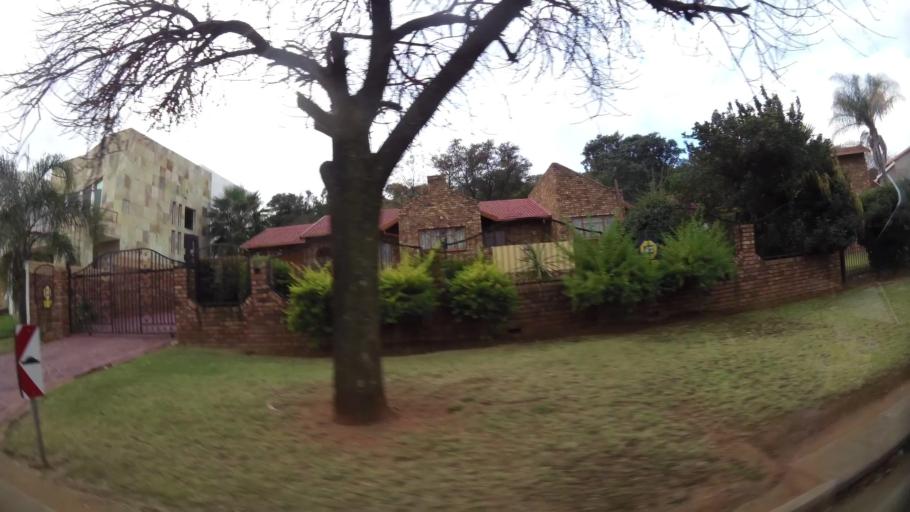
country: ZA
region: Gauteng
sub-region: City of Tshwane Metropolitan Municipality
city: Pretoria
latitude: -25.6977
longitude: 28.3079
